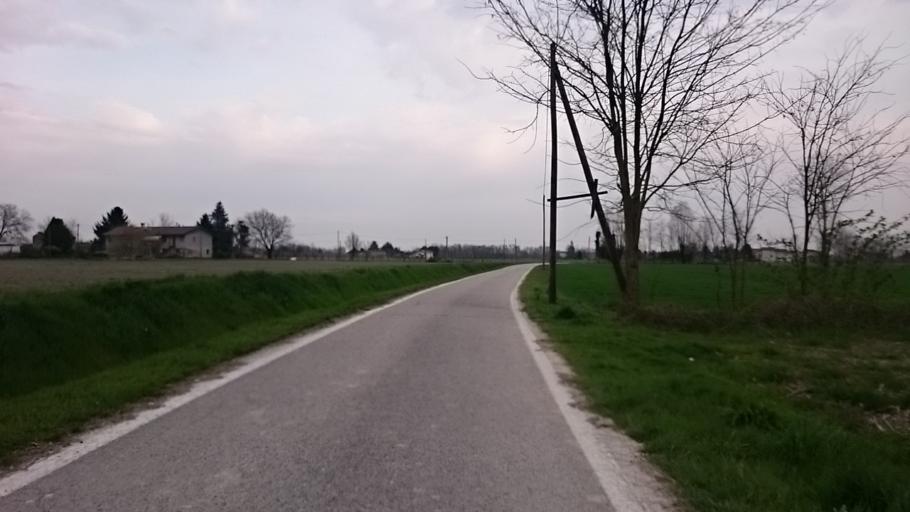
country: IT
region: Veneto
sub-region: Provincia di Padova
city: Tremignon
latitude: 45.5287
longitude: 11.8068
